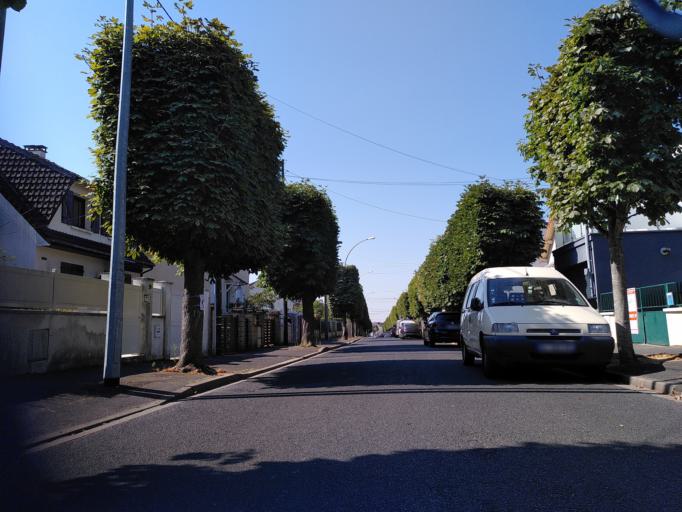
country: FR
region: Ile-de-France
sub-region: Departement de l'Essonne
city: Savigny-sur-Orge
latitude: 48.6879
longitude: 2.3485
